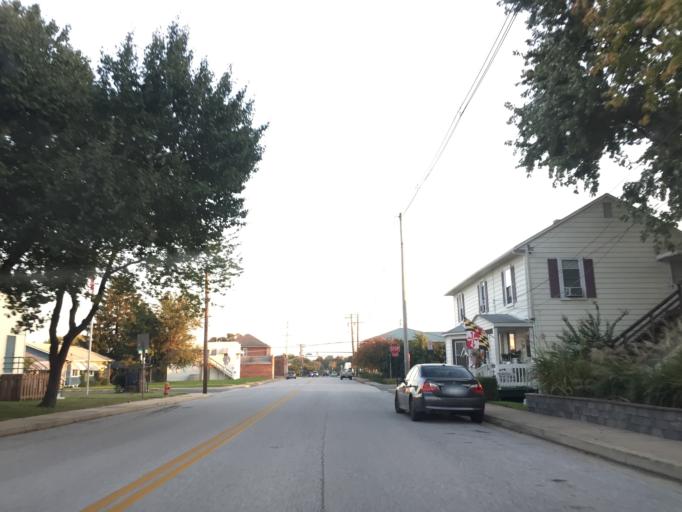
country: US
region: Maryland
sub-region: Baltimore County
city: Essex
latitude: 39.3106
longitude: -76.4746
